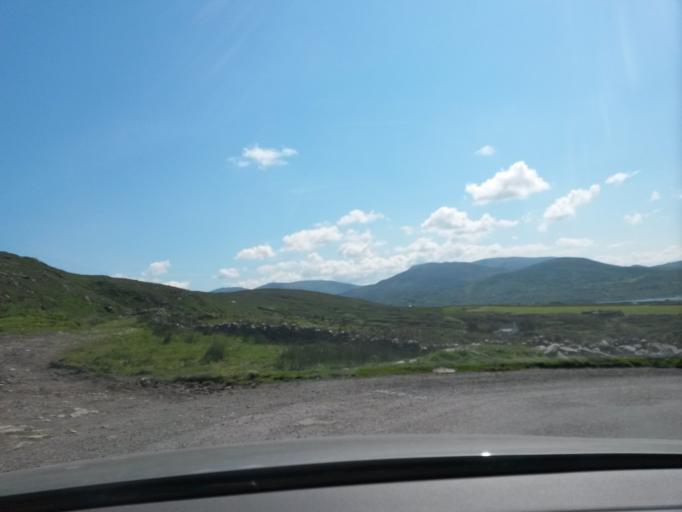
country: IE
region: Munster
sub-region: Ciarrai
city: Cahersiveen
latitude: 51.7226
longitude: -9.9835
